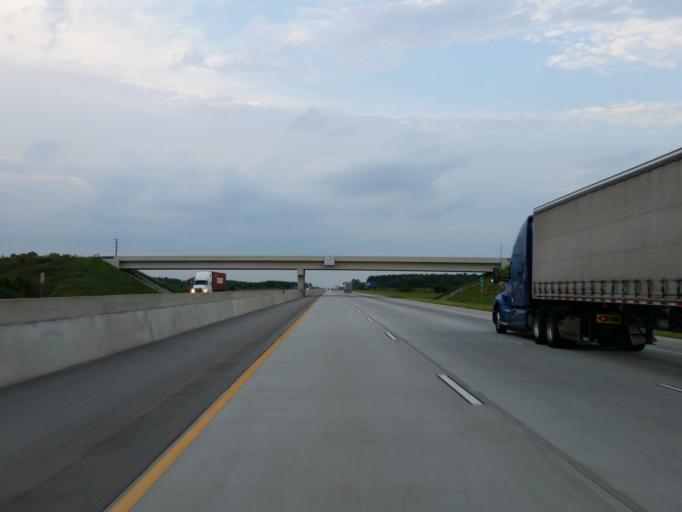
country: US
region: Georgia
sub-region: Tift County
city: Unionville
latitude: 31.3319
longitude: -83.4832
